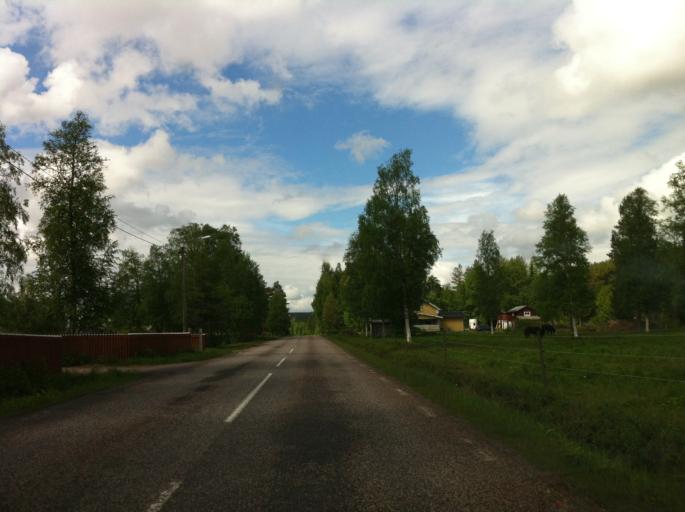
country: SE
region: Dalarna
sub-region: Malung-Saelens kommun
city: Malung
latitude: 61.2006
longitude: 13.2273
